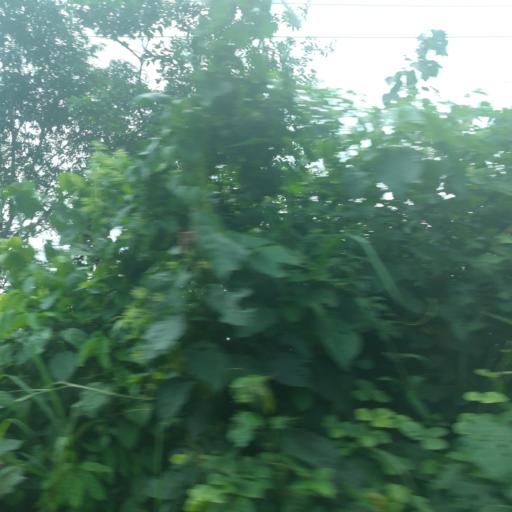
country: NG
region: Lagos
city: Ejirin
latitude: 6.6545
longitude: 3.7217
